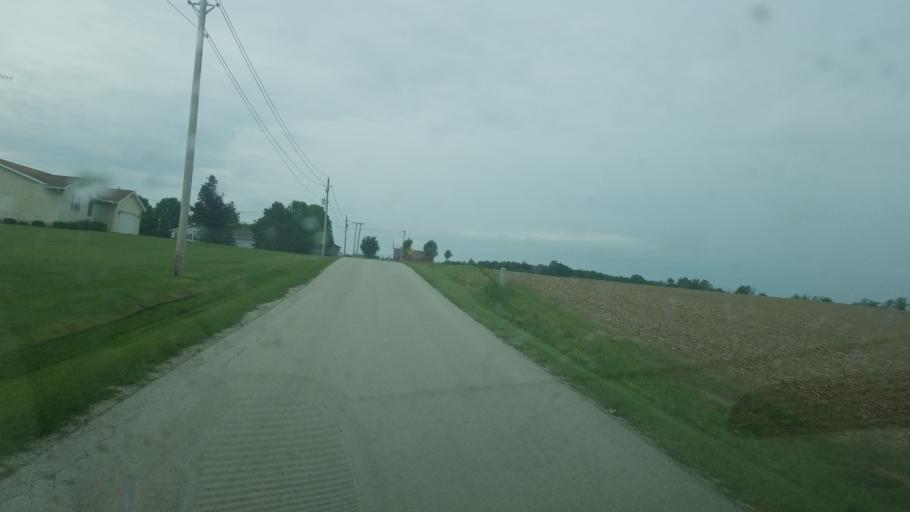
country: US
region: Ohio
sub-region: Crawford County
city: Crestline
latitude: 40.8502
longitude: -82.8276
